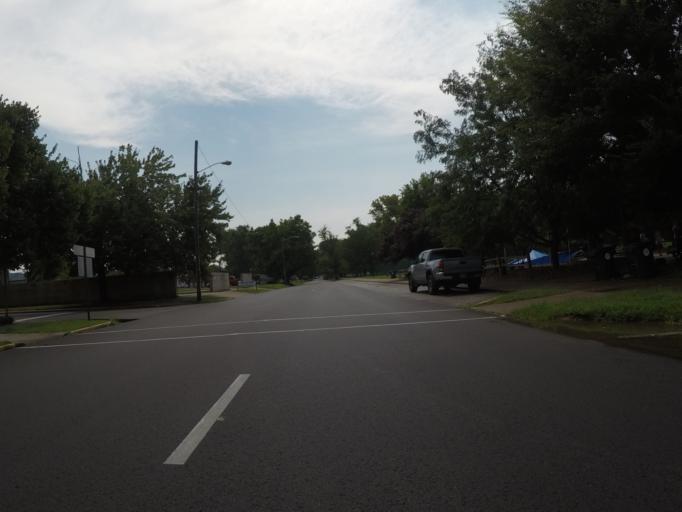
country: US
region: Kentucky
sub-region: Boyd County
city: Ashland
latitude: 38.4757
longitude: -82.6389
